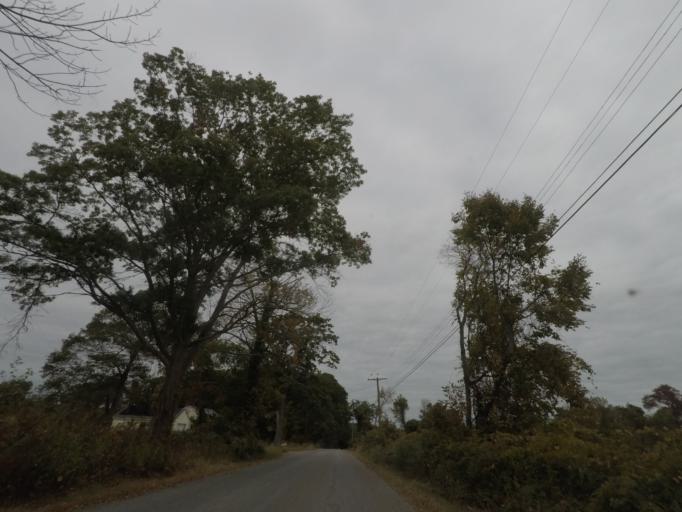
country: US
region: Connecticut
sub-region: Windham County
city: Thompson
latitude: 41.9537
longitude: -71.8338
